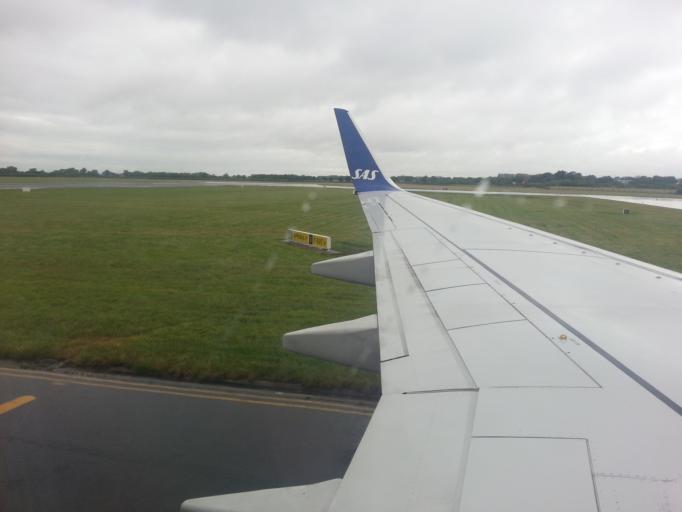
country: IE
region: Leinster
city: Ballymun
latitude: 53.4341
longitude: -6.2580
